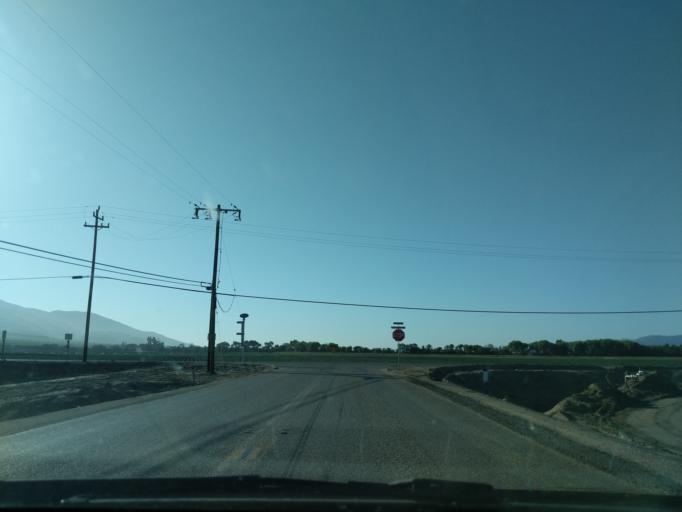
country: US
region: California
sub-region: Monterey County
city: Gonzales
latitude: 36.4728
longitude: -121.4742
